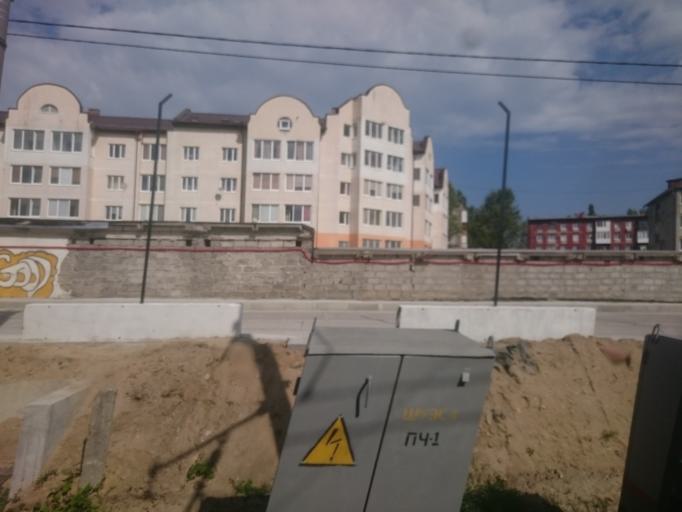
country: RU
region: Kaliningrad
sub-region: Zelenogradskiy Rayon
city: Zelenogradsk
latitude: 54.9517
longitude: 20.4636
